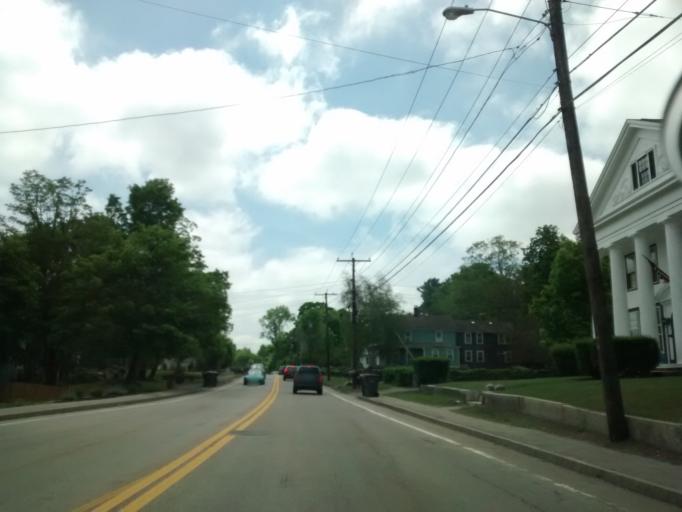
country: US
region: Massachusetts
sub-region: Worcester County
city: Grafton
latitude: 42.2277
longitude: -71.7076
